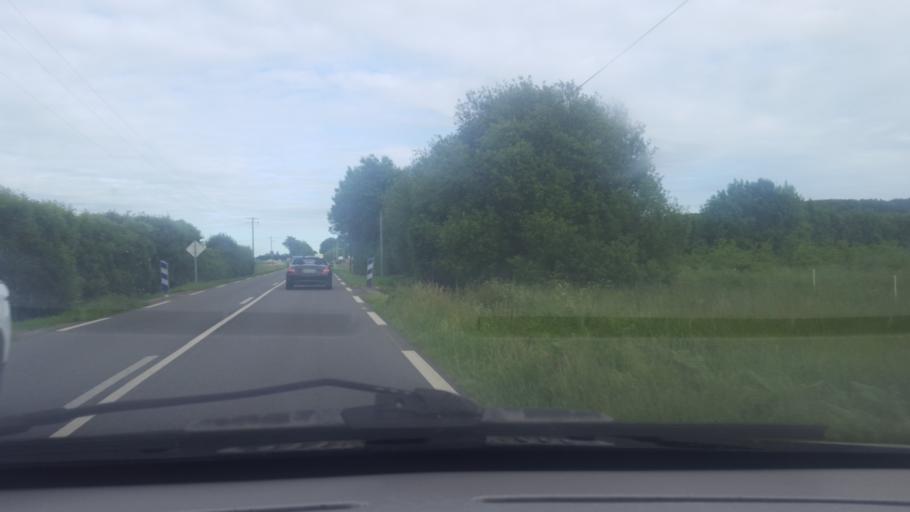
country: FR
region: Pays de la Loire
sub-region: Departement de la Loire-Atlantique
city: Machecoul
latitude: 47.0097
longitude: -1.8494
